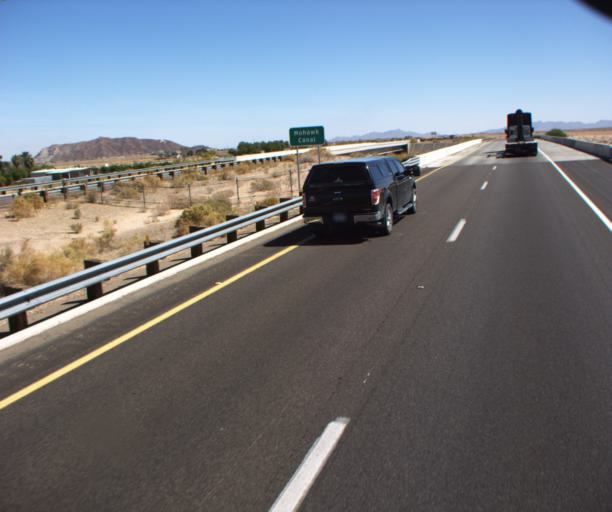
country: US
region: Arizona
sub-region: Yuma County
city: Wellton
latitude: 32.6762
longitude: -114.0493
